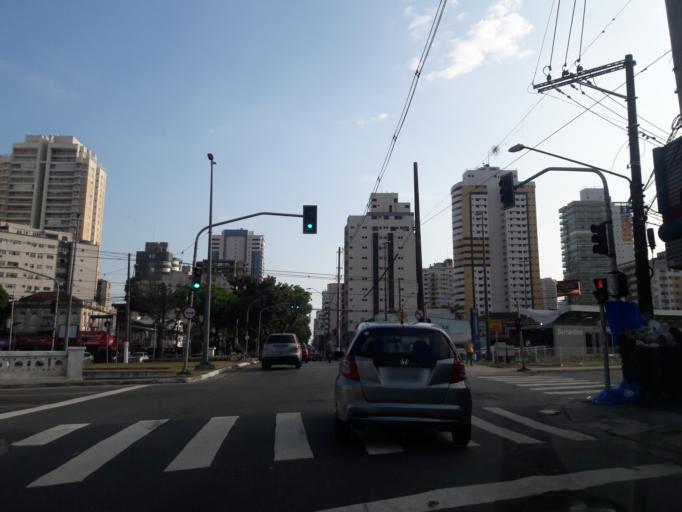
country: BR
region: Sao Paulo
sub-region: Santos
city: Santos
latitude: -23.9611
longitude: -46.3384
